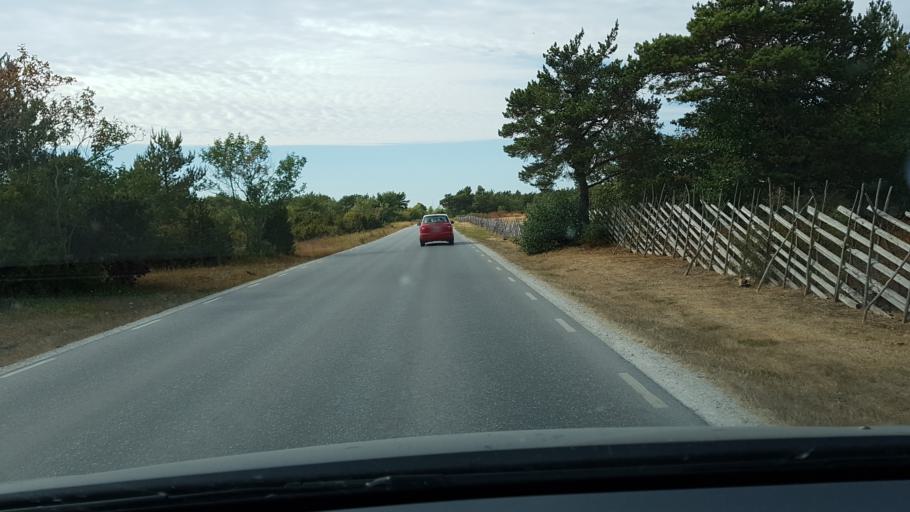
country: SE
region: Gotland
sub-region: Gotland
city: Visby
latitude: 57.6499
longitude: 18.3231
